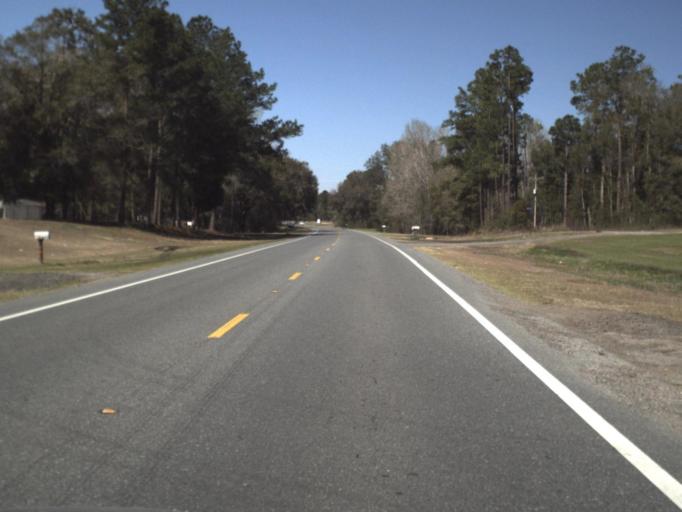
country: US
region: Florida
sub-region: Jackson County
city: Marianna
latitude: 30.7303
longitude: -85.0905
